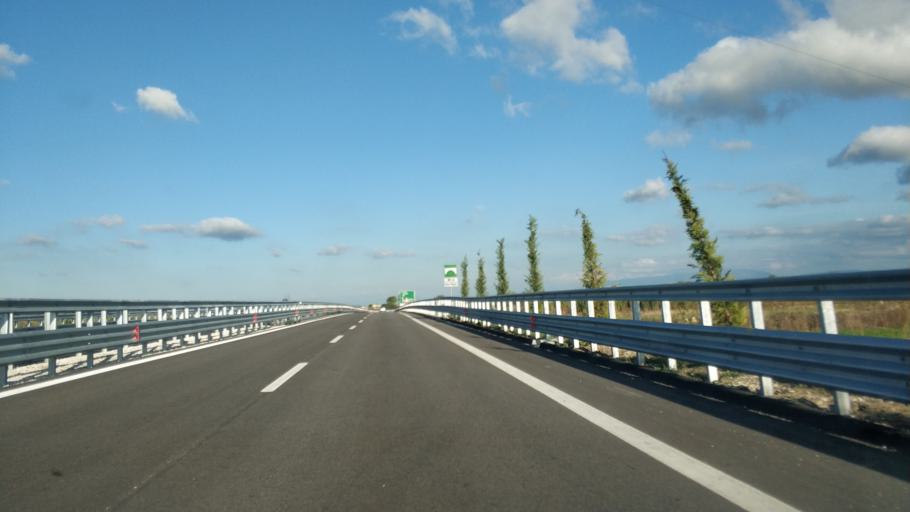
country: AL
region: Fier
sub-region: Rrethi i Fierit
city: Dermenas
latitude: 40.7403
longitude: 19.4698
